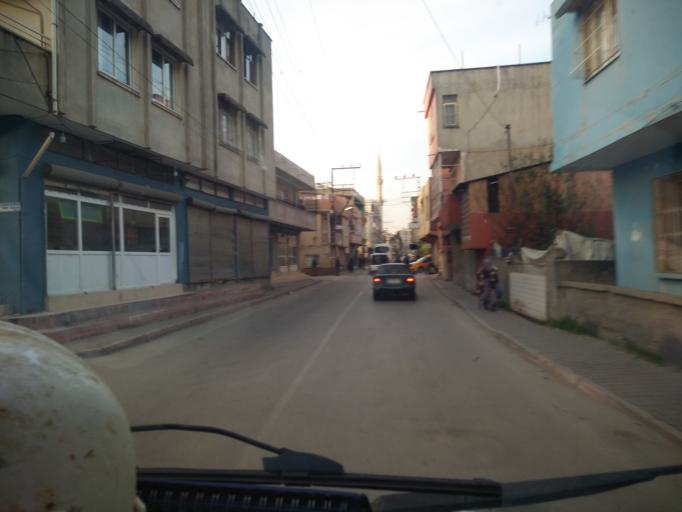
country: TR
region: Adana
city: Seyhan
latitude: 37.0010
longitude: 35.2799
